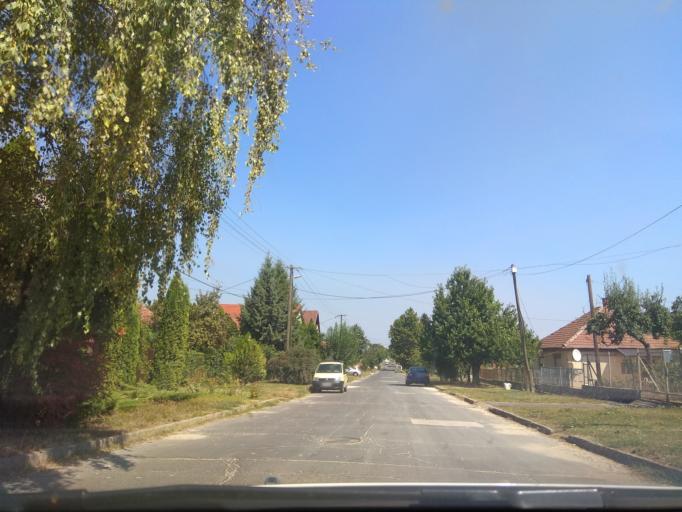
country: HU
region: Borsod-Abauj-Zemplen
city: Miskolc
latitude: 48.0664
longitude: 20.7770
